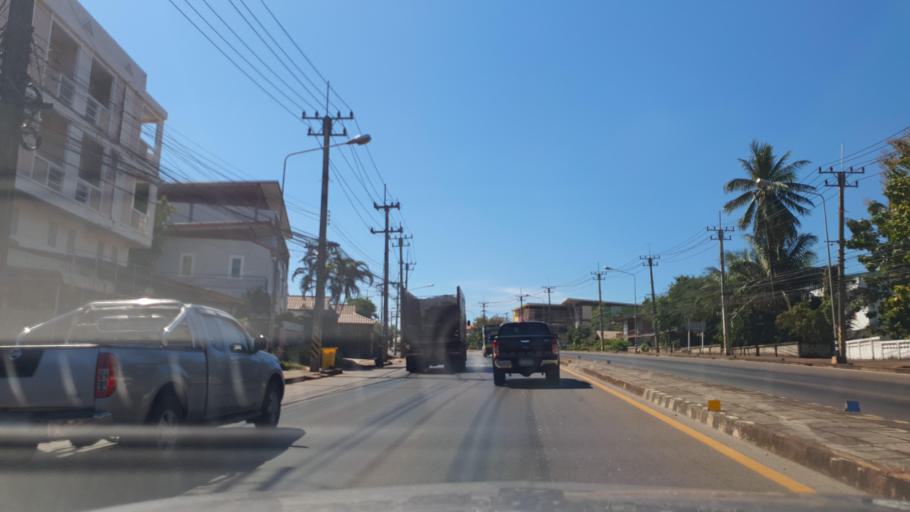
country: TH
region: Sakon Nakhon
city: Sakon Nakhon
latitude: 17.1885
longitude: 104.0935
